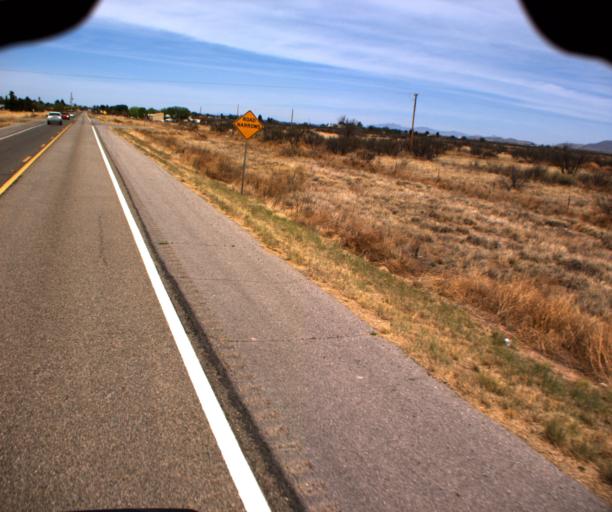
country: US
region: Arizona
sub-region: Cochise County
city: Bisbee
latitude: 31.6697
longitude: -109.6822
